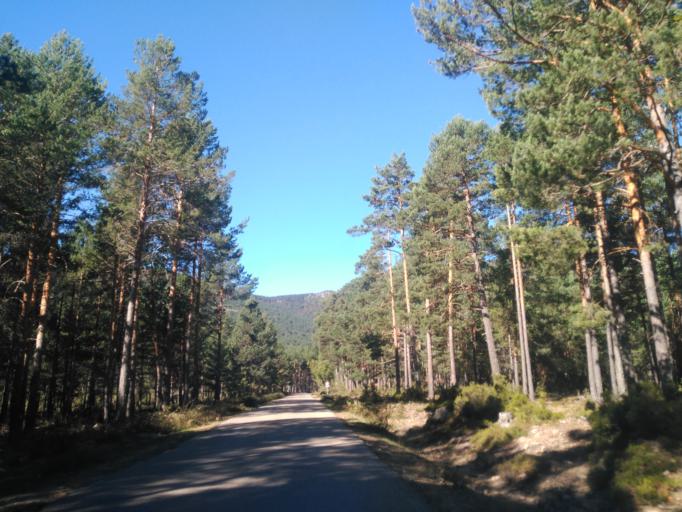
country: ES
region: Castille and Leon
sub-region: Provincia de Soria
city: Vinuesa
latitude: 41.9753
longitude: -2.7869
